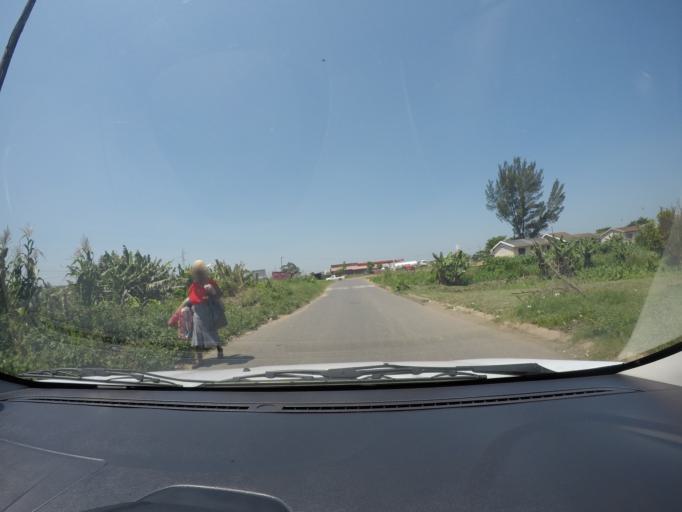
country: ZA
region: KwaZulu-Natal
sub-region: uThungulu District Municipality
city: eSikhawini
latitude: -28.8688
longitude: 31.9049
